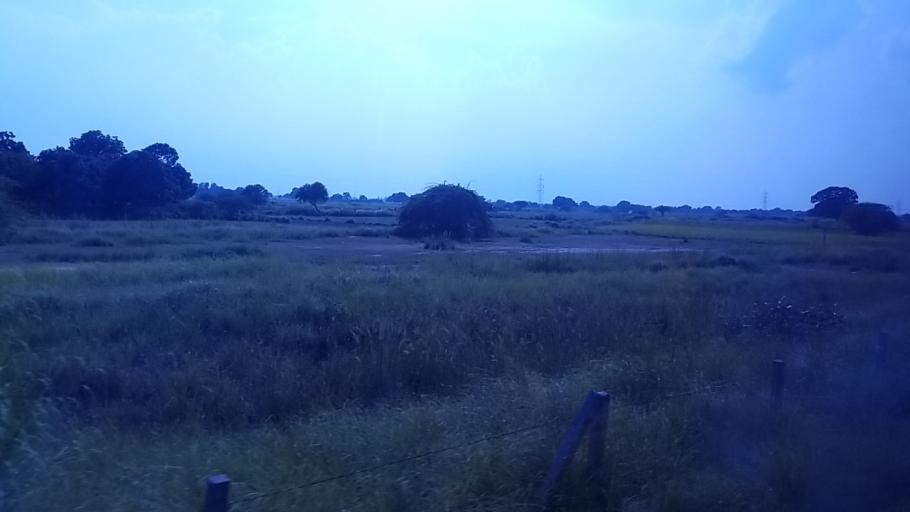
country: IN
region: Uttar Pradesh
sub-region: Fatehpur
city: Khaga
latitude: 25.7239
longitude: 81.1758
